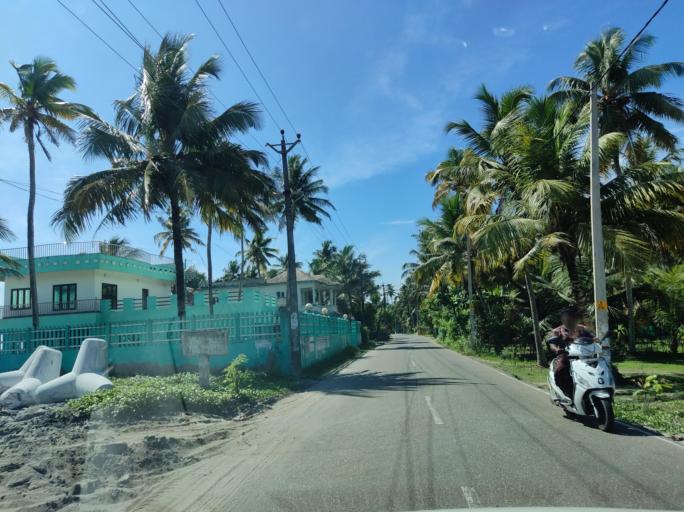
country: IN
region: Kerala
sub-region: Alappuzha
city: Kayankulam
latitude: 9.1942
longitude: 76.4372
